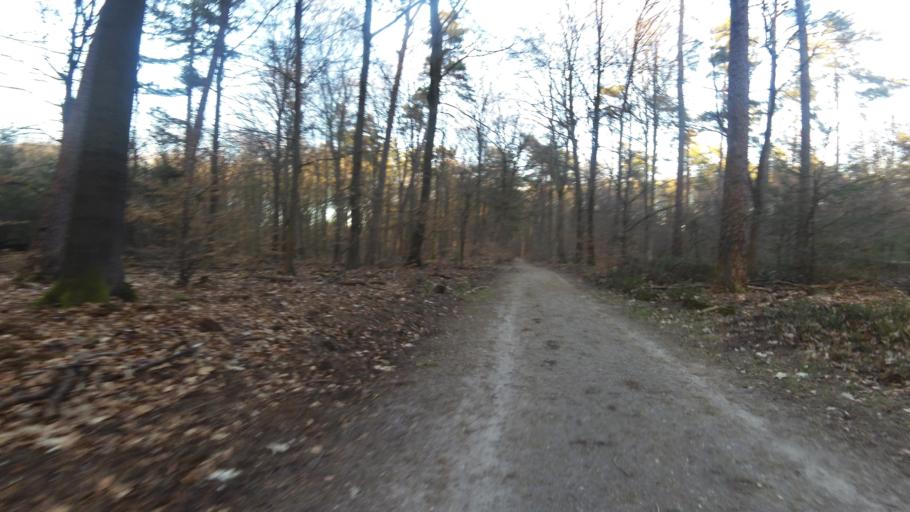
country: NL
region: Gelderland
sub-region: Gemeente Putten
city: Putten
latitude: 52.2467
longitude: 5.6546
